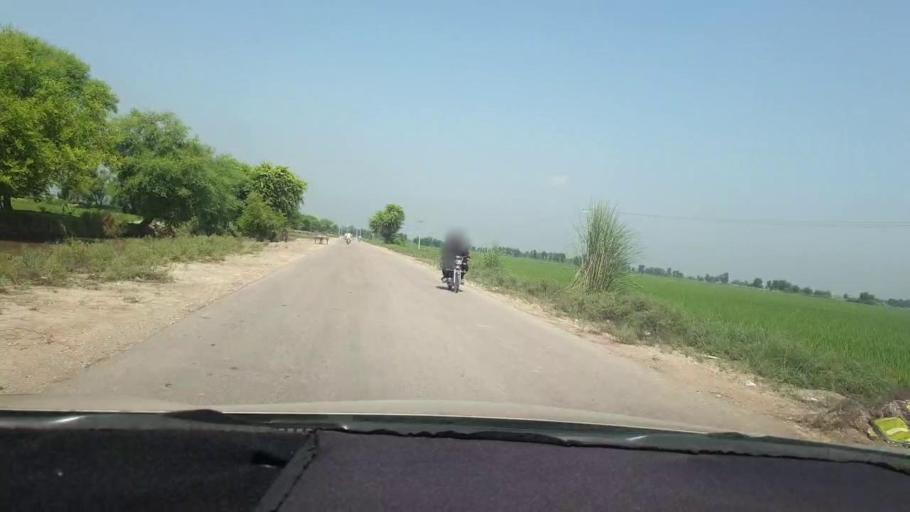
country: PK
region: Sindh
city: Miro Khan
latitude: 27.7653
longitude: 68.0726
